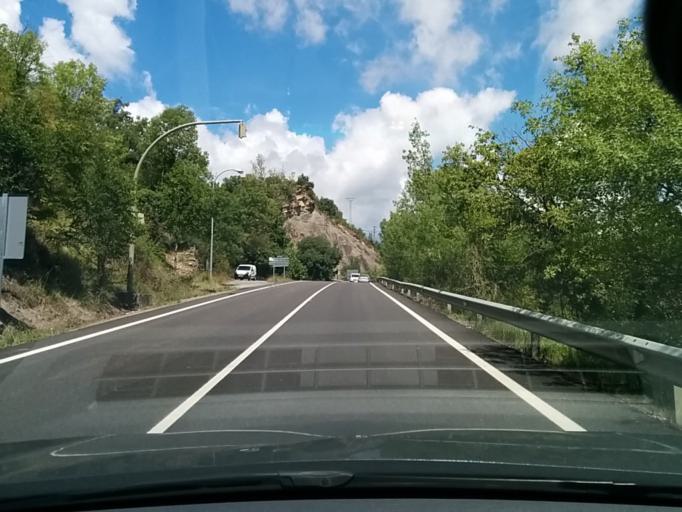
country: ES
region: Aragon
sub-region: Provincia de Huesca
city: Ainsa
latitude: 42.4173
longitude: 0.1403
